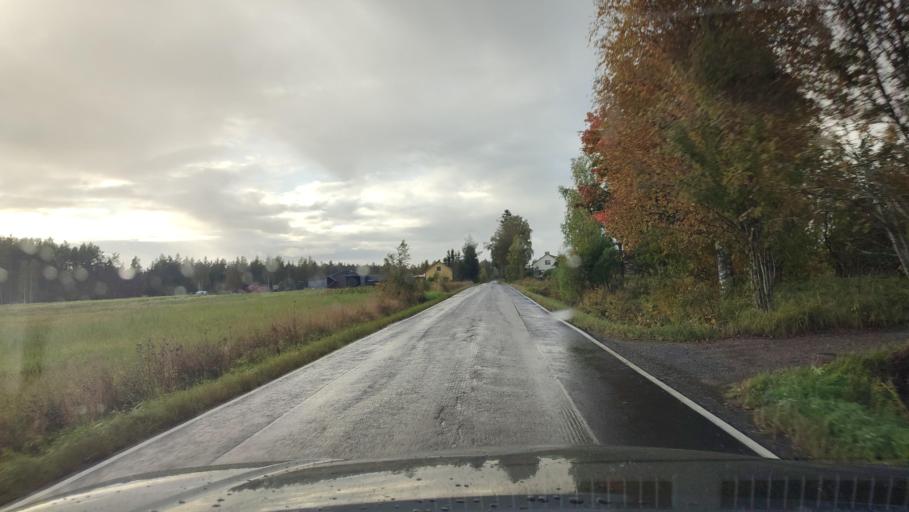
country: FI
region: Southern Ostrobothnia
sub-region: Suupohja
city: Karijoki
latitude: 62.3145
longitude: 21.6964
